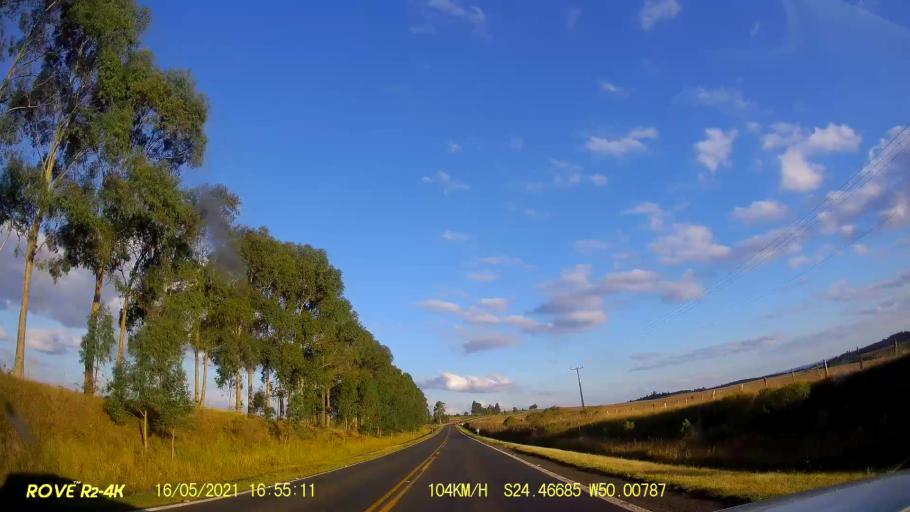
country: BR
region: Parana
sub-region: Pirai Do Sul
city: Pirai do Sul
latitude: -24.4669
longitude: -50.0078
